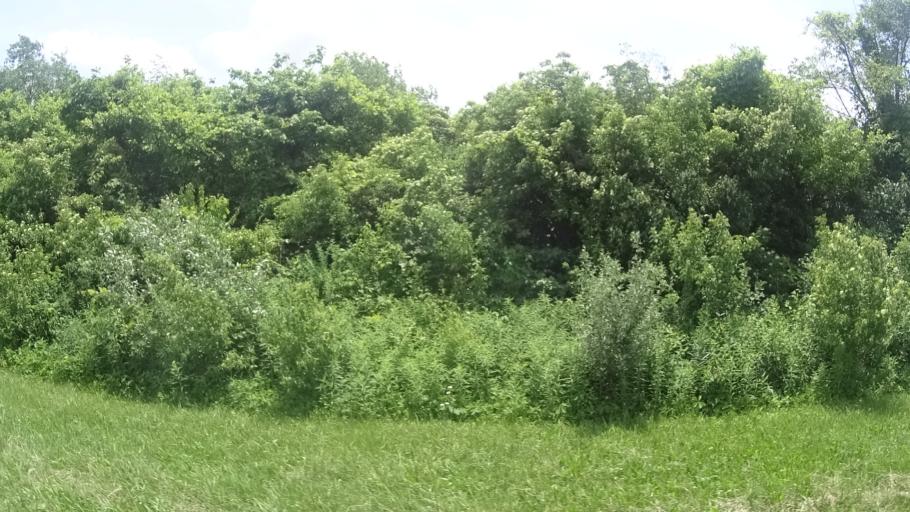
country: US
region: Ohio
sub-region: Huron County
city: Bellevue
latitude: 41.2982
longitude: -82.7725
